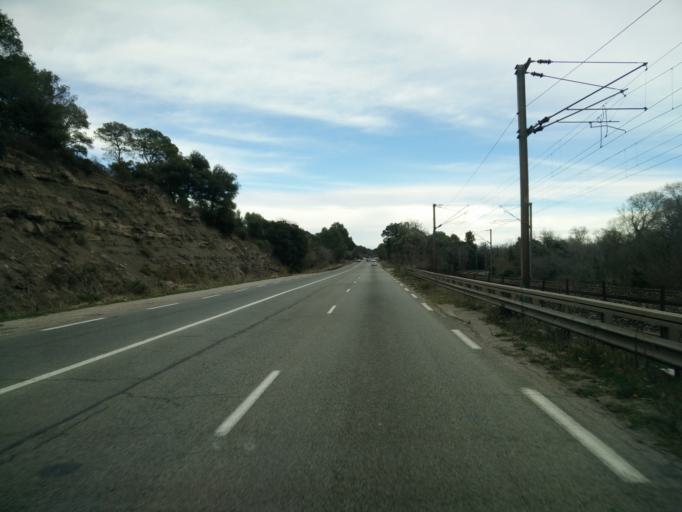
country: FR
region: Provence-Alpes-Cote d'Azur
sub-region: Departement du Var
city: Roquebrune-sur-Argens
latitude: 43.4670
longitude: 6.6123
